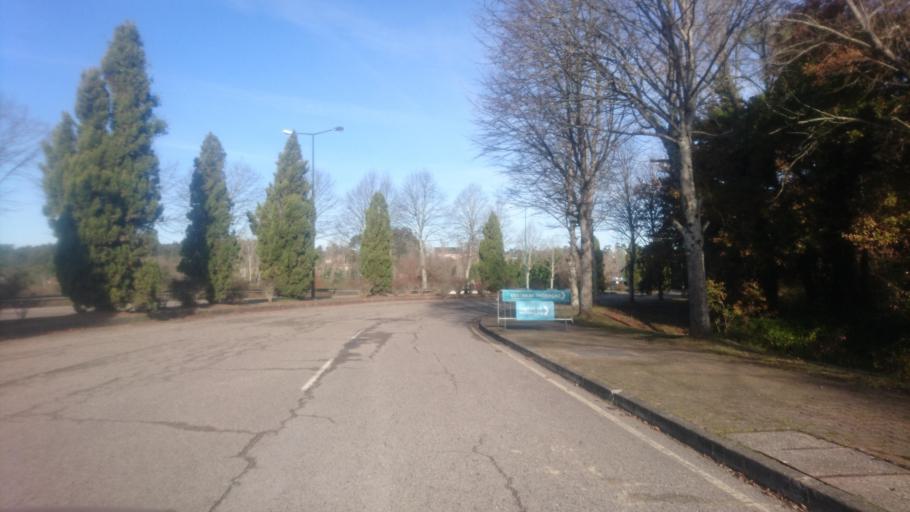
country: PT
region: Aveiro
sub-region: Santa Maria da Feira
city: Rio Meao
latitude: 40.9292
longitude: -8.5769
